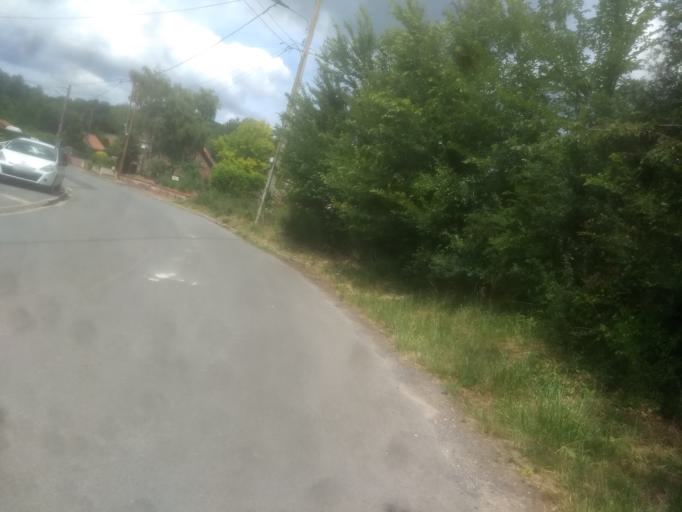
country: FR
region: Nord-Pas-de-Calais
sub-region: Departement du Pas-de-Calais
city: Mont-Saint-Eloi
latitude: 50.3371
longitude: 2.6919
